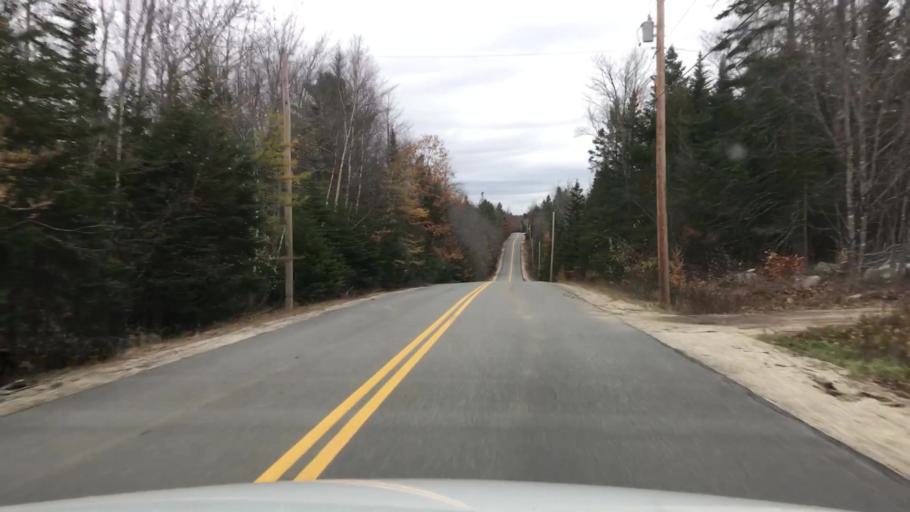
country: US
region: Maine
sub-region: Hancock County
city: Penobscot
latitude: 44.4486
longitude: -68.6368
